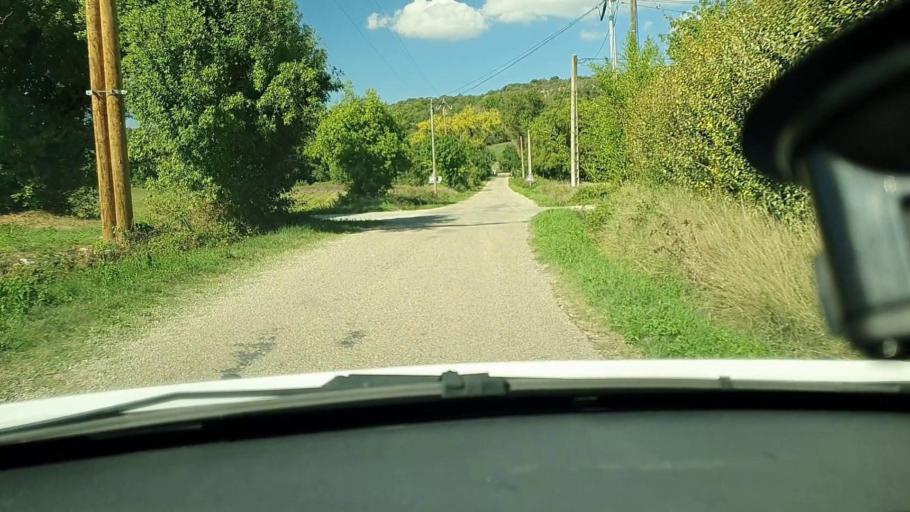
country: FR
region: Languedoc-Roussillon
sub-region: Departement du Gard
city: Goudargues
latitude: 44.1711
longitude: 4.3856
